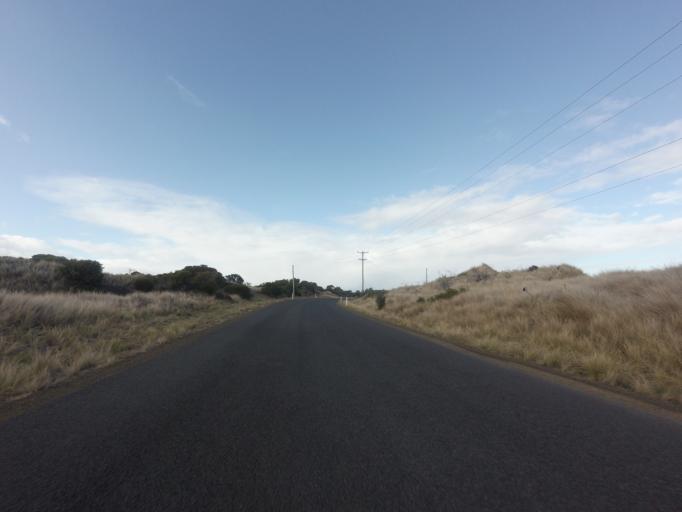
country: AU
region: Tasmania
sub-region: Break O'Day
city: St Helens
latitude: -42.0885
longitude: 148.1534
